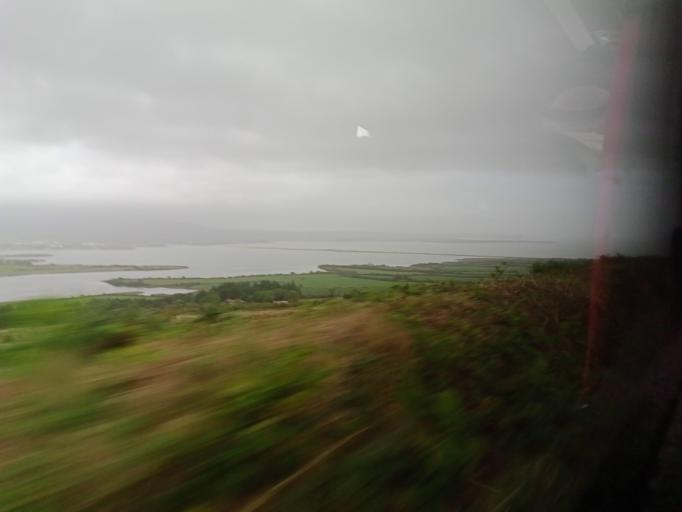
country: IE
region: Munster
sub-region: Waterford
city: Dungarvan
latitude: 52.0515
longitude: -7.6378
